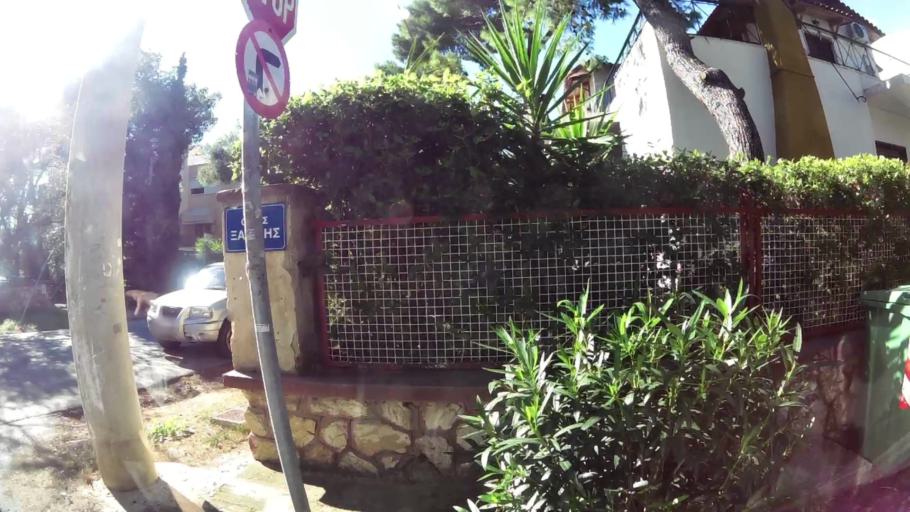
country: GR
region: Attica
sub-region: Nomarchia Athinas
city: Nea Erythraia
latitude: 38.0922
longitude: 23.8052
